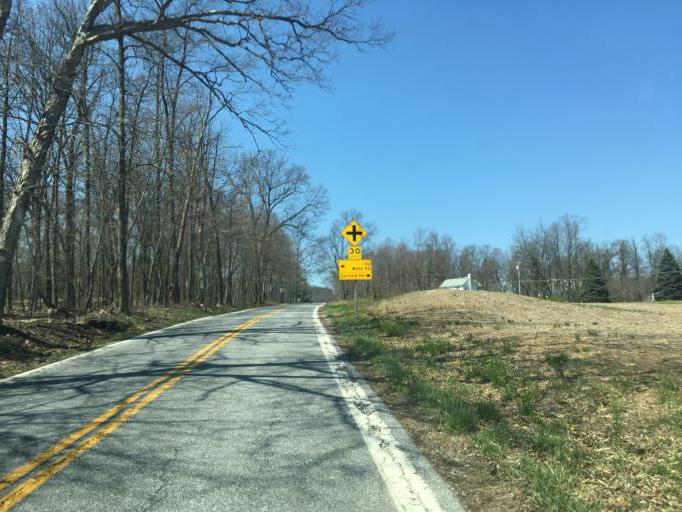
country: US
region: Maryland
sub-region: Washington County
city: Cavetown
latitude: 39.6214
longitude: -77.5579
